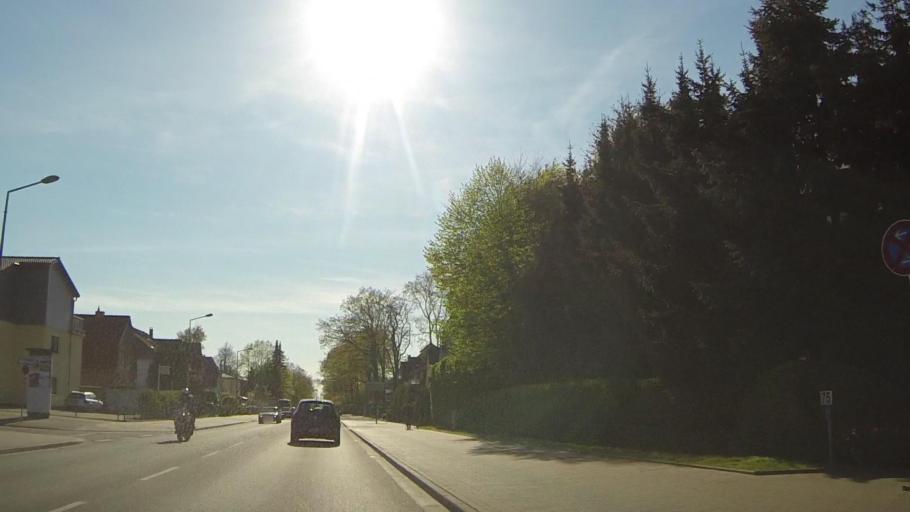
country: DE
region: Schleswig-Holstein
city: Wedel
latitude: 53.5832
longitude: 9.7195
